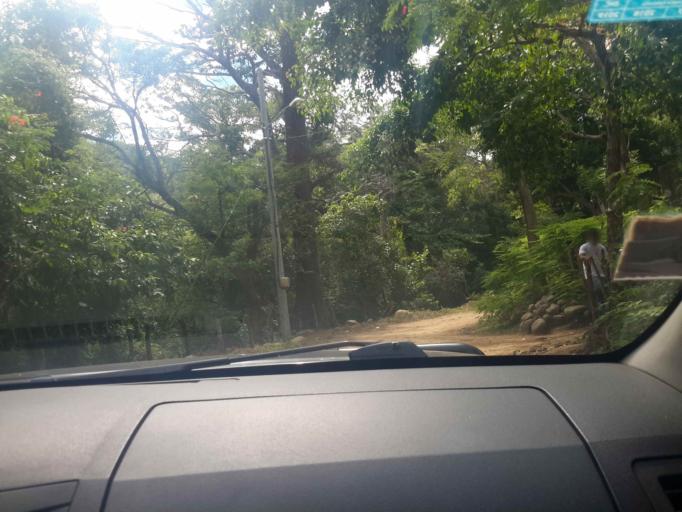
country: NI
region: Carazo
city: Santa Teresa
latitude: 11.6554
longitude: -86.1888
